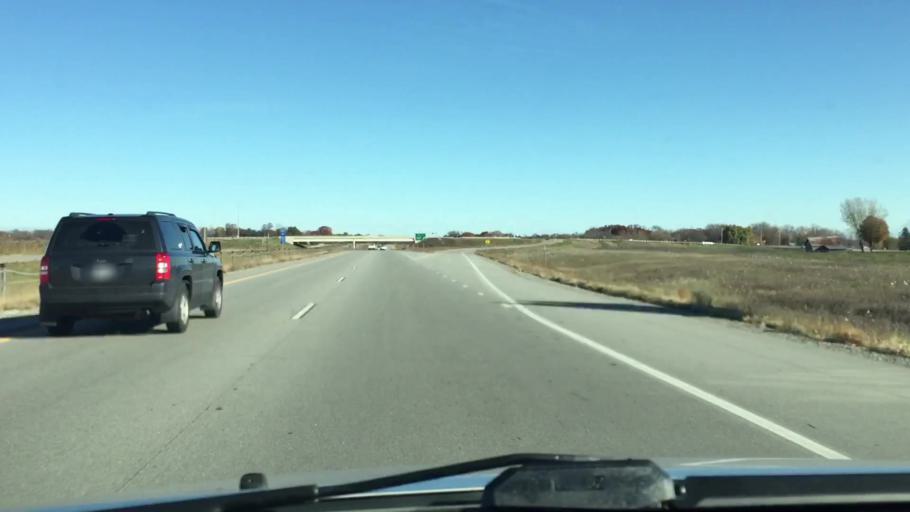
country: US
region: Wisconsin
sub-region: Brown County
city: Wrightstown
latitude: 44.3823
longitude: -88.1643
